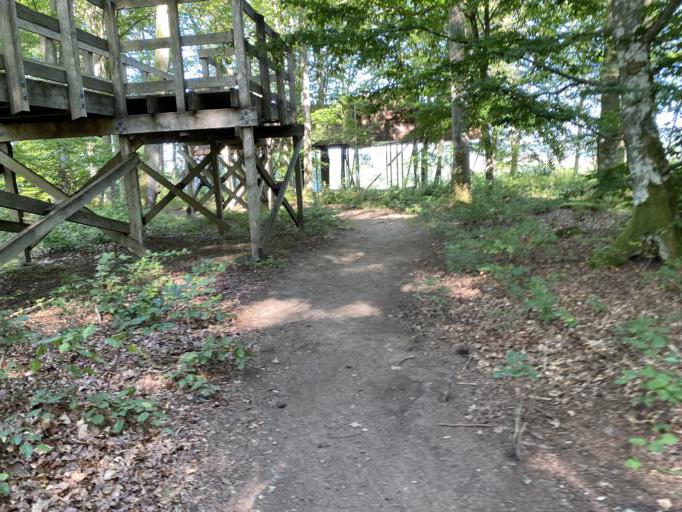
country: SE
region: Skane
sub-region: Hassleholms Kommun
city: Tormestorp
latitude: 56.1140
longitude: 13.6972
